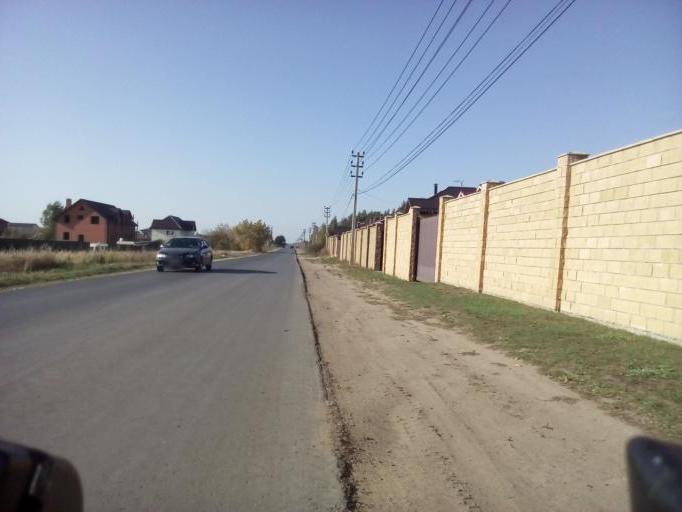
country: RU
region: Moskovskaya
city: Ramenskoye
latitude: 55.5606
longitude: 38.3070
